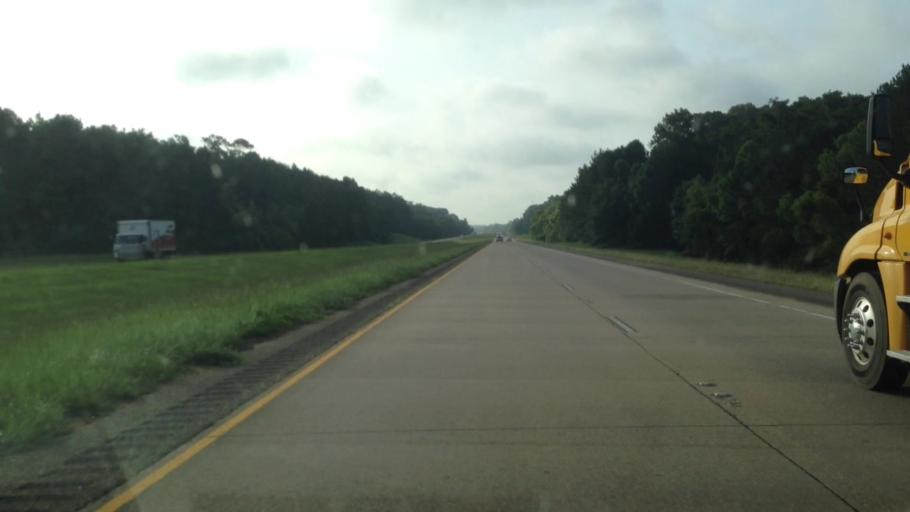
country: US
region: Louisiana
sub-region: Rapides Parish
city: Lecompte
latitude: 31.0260
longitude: -92.4010
